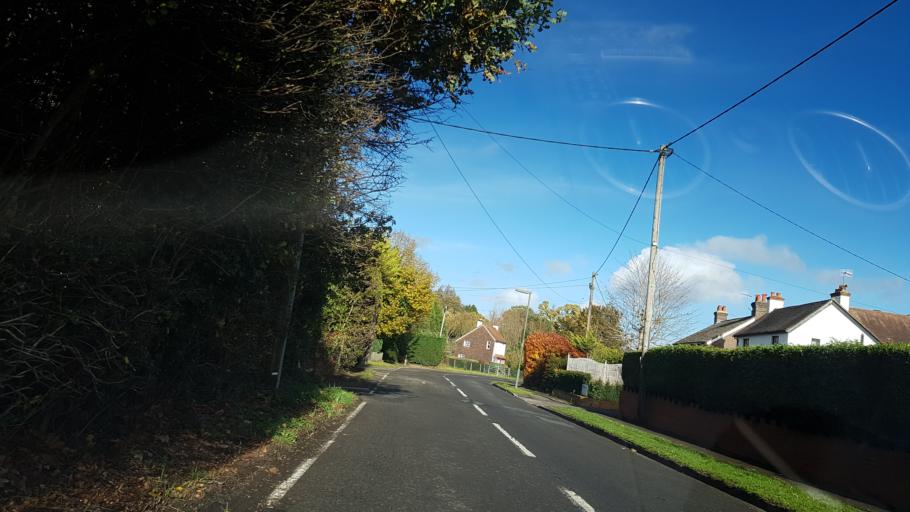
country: GB
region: England
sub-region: Surrey
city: Elstead
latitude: 51.1757
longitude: -0.7127
